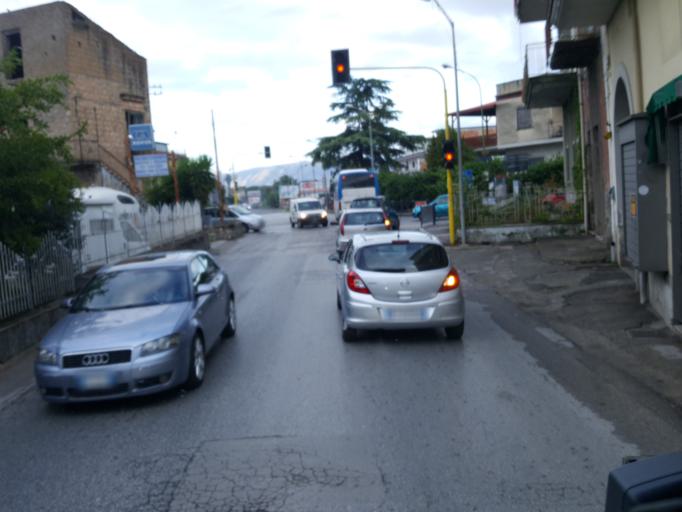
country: IT
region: Campania
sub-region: Provincia di Napoli
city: Palma Campania
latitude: 40.8796
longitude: 14.5506
